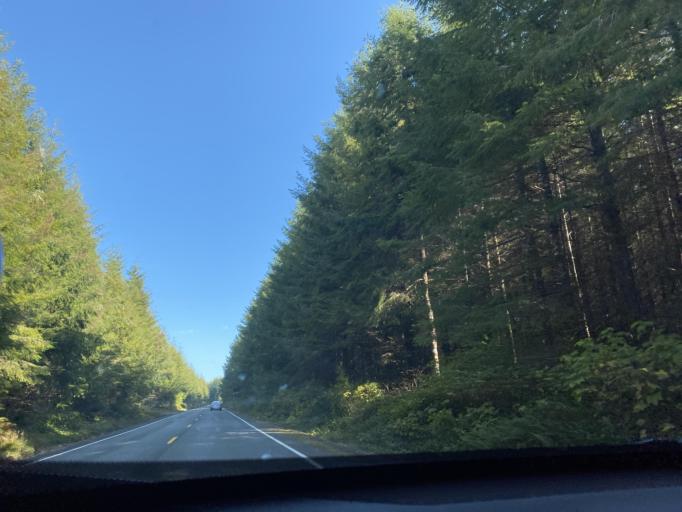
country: US
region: Washington
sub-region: Clallam County
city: Forks
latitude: 47.9209
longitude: -124.5083
